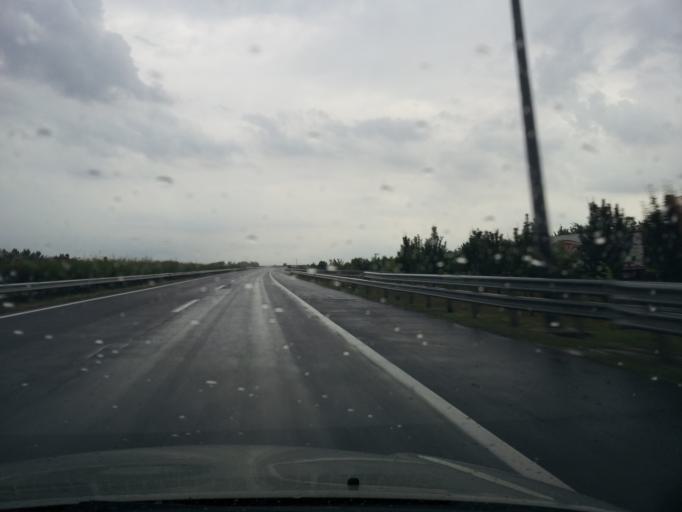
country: HU
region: Borsod-Abauj-Zemplen
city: Onod
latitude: 47.9627
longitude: 20.8937
